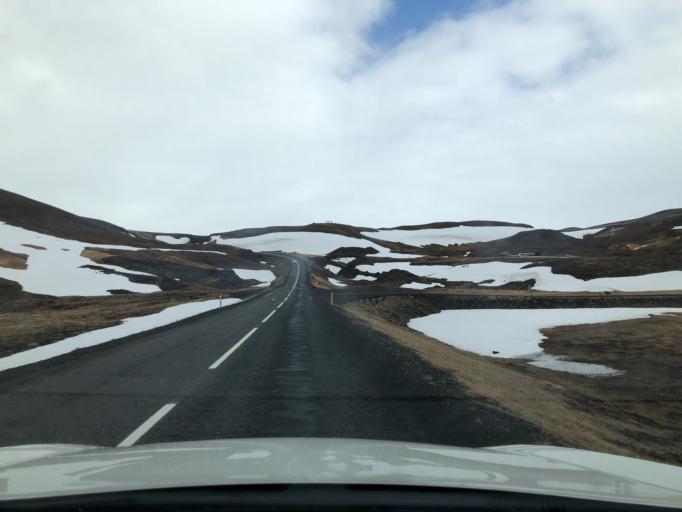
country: IS
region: Northeast
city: Laugar
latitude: 65.7062
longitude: -16.7719
